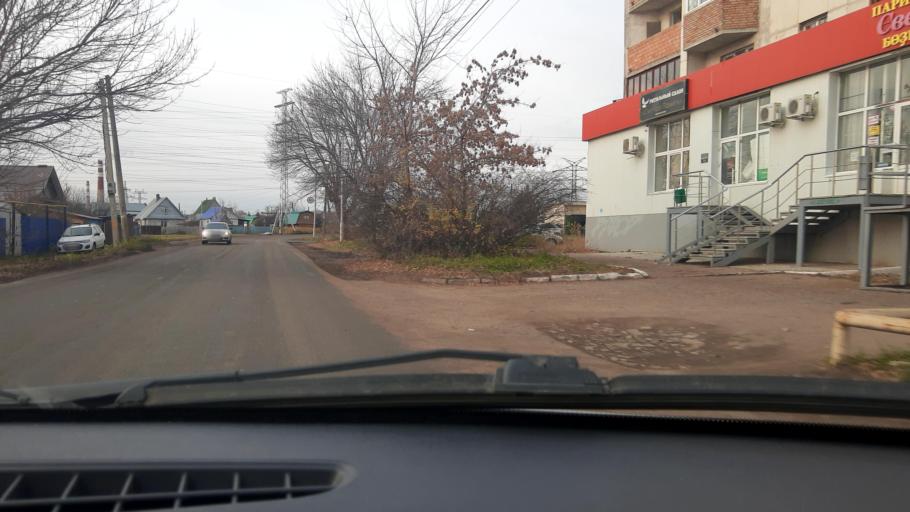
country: RU
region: Bashkortostan
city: Avdon
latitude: 54.6942
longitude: 55.8194
